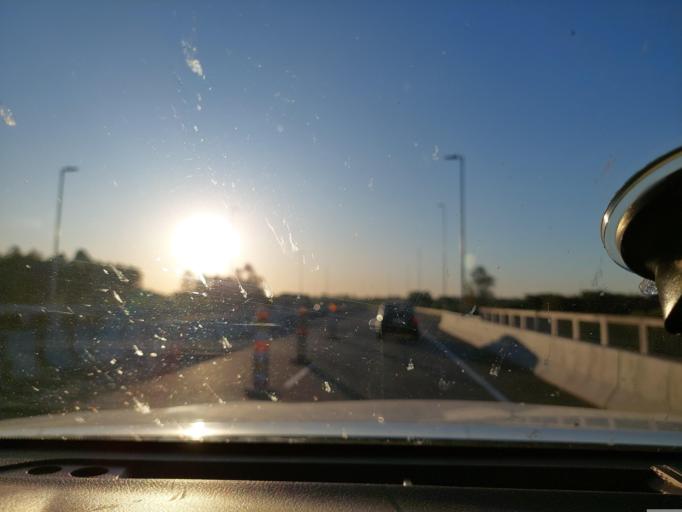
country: UY
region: Canelones
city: Pando
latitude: -34.7127
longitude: -55.9402
